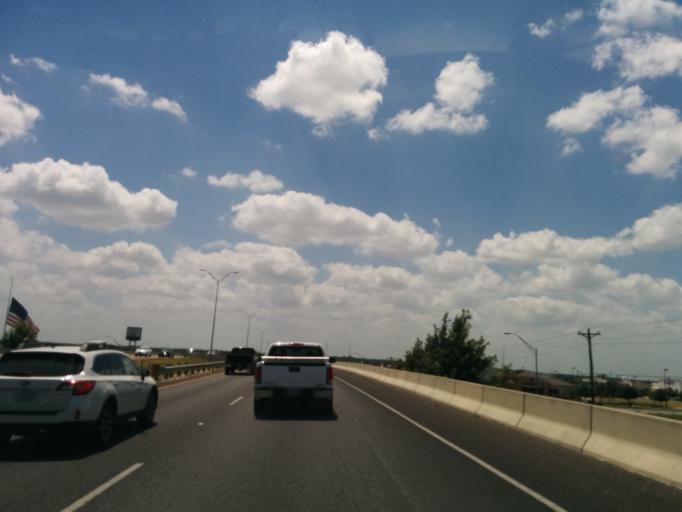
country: US
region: Texas
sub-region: Bastrop County
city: Bastrop
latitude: 30.1113
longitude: -97.3486
